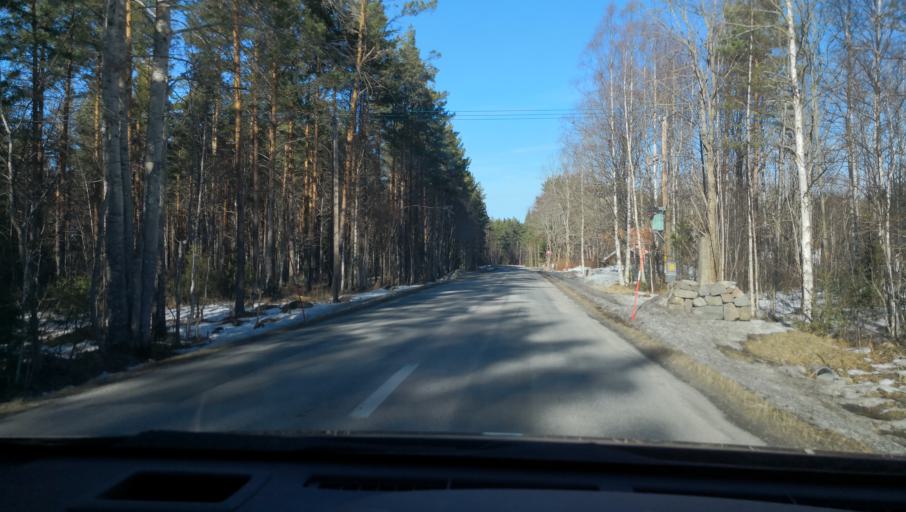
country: SE
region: Uppsala
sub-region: Osthammars Kommun
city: Osterbybruk
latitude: 60.2663
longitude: 17.9554
